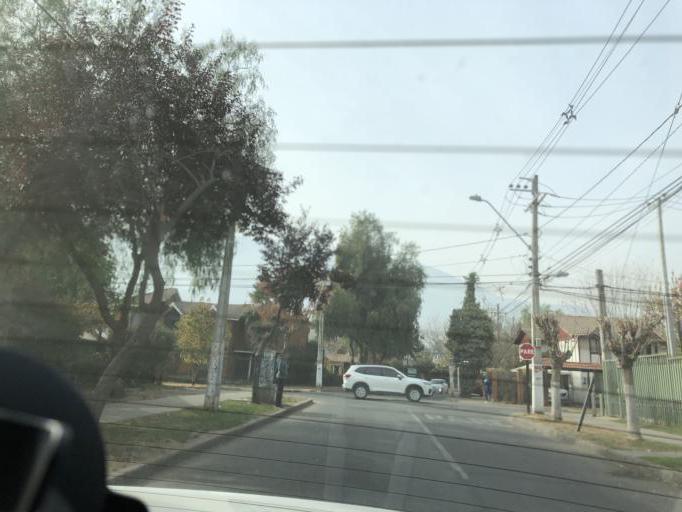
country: CL
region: Santiago Metropolitan
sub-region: Provincia de Cordillera
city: Puente Alto
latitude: -33.5493
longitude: -70.5580
